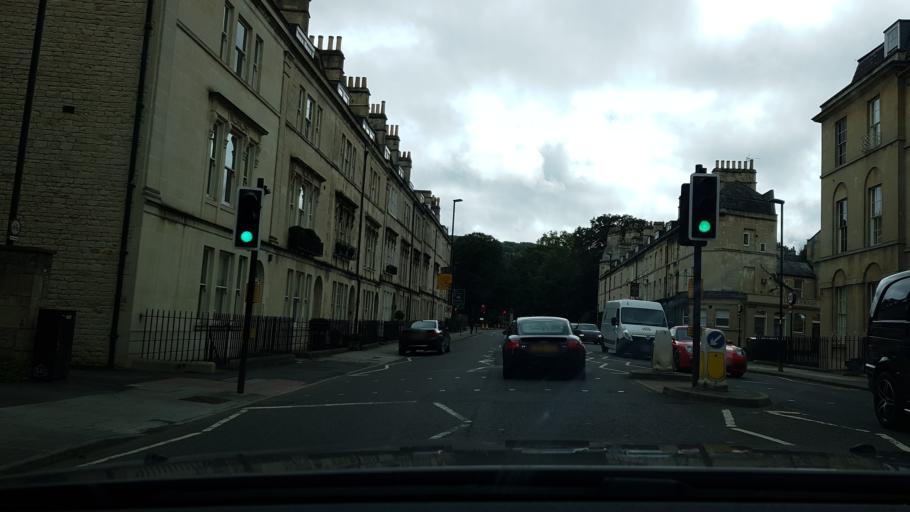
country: GB
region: England
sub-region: Bath and North East Somerset
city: Bath
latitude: 51.3874
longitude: -2.3530
